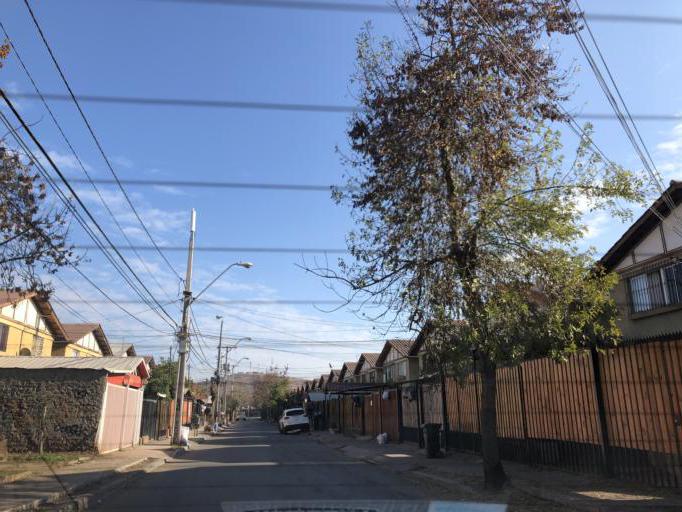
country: CL
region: Santiago Metropolitan
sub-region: Provincia de Cordillera
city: Puente Alto
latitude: -33.6309
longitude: -70.5931
